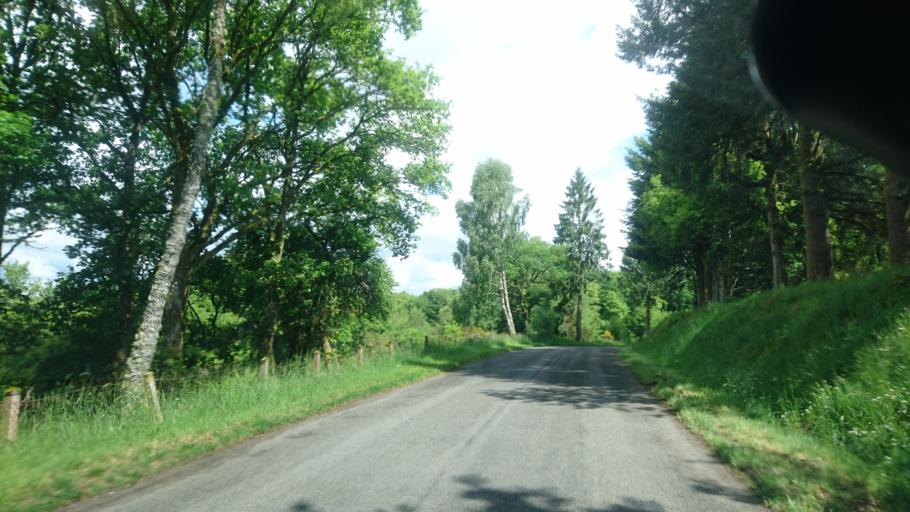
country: FR
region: Limousin
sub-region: Departement de la Haute-Vienne
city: Peyrat-le-Chateau
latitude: 45.7779
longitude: 1.8736
